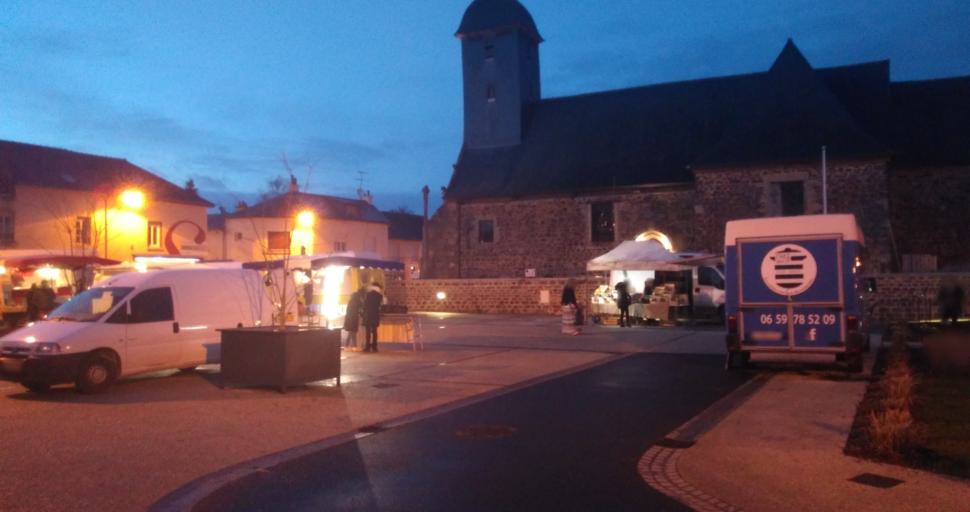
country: FR
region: Brittany
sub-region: Departement d'Ille-et-Vilaine
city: Pleumeleuc
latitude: 48.1842
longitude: -1.9187
